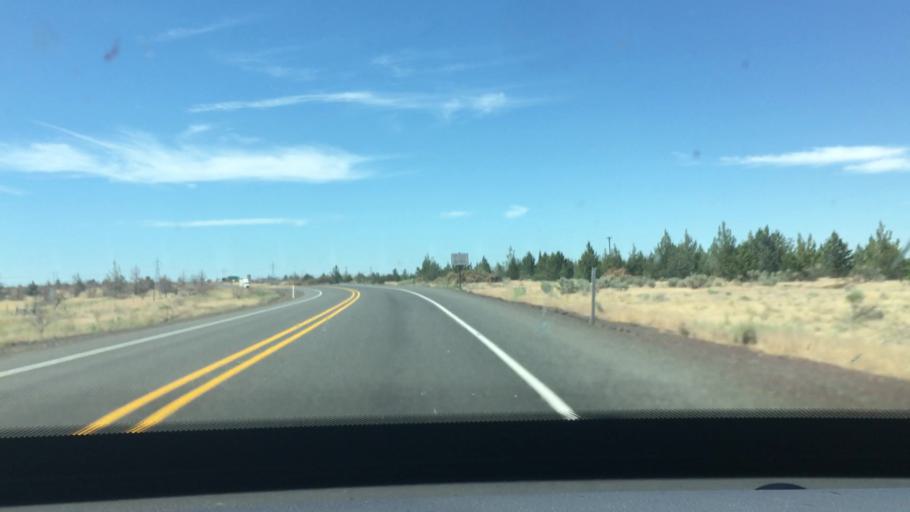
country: US
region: Oregon
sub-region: Jefferson County
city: Madras
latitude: 44.9114
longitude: -120.9402
